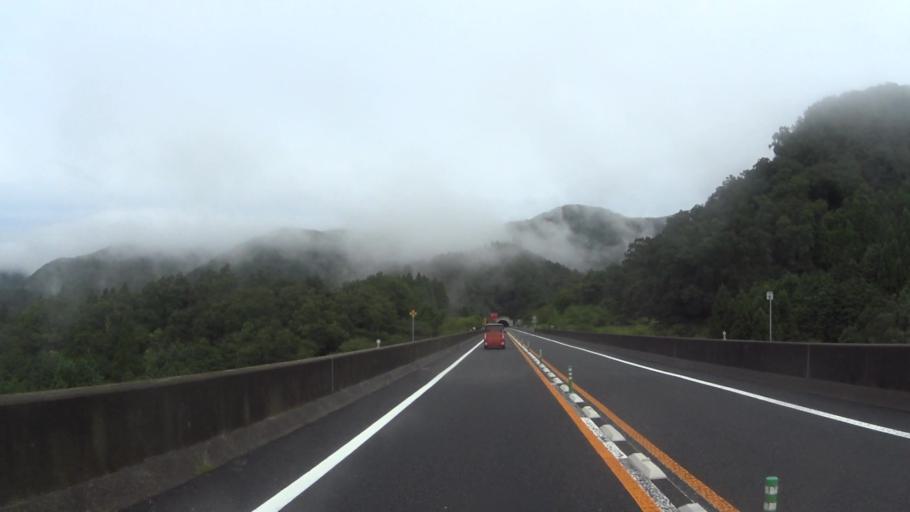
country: JP
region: Kyoto
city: Ayabe
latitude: 35.2062
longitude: 135.3531
